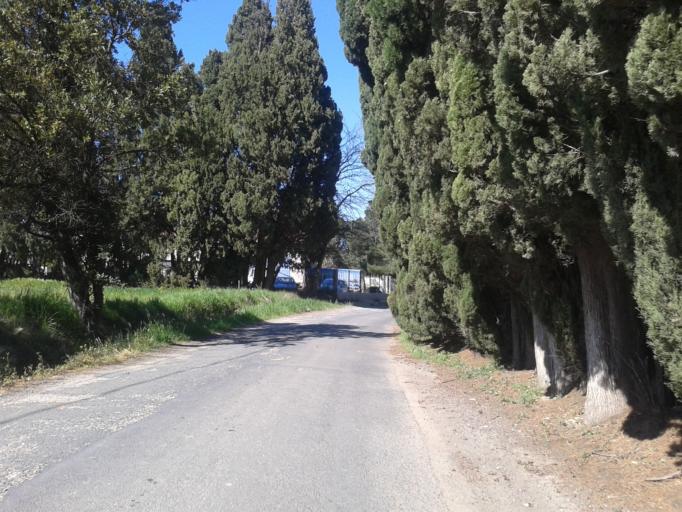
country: FR
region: Languedoc-Roussillon
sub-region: Departement des Pyrenees-Orientales
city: Pezilla-la-Riviere
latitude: 42.6996
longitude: 2.7712
